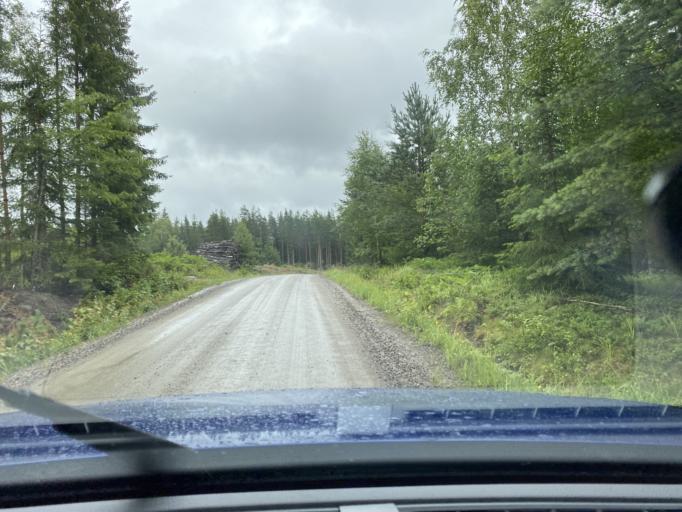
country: FI
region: Pirkanmaa
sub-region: Lounais-Pirkanmaa
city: Punkalaidun
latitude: 61.1480
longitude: 23.2592
